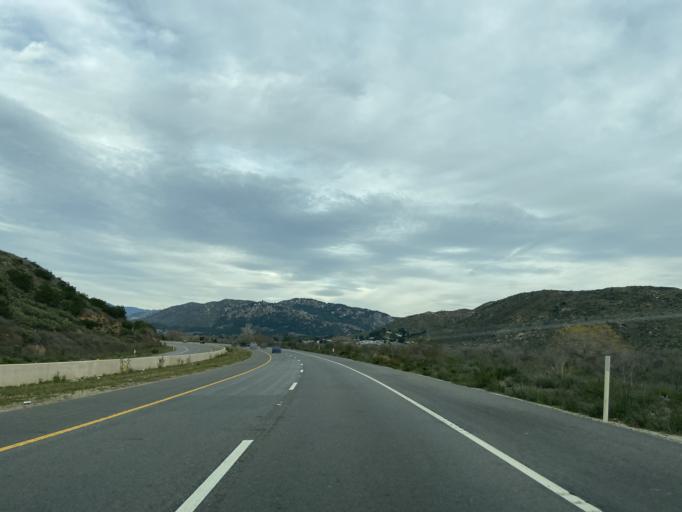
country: US
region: California
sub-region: San Diego County
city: Bonsall
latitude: 33.3153
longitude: -117.1794
